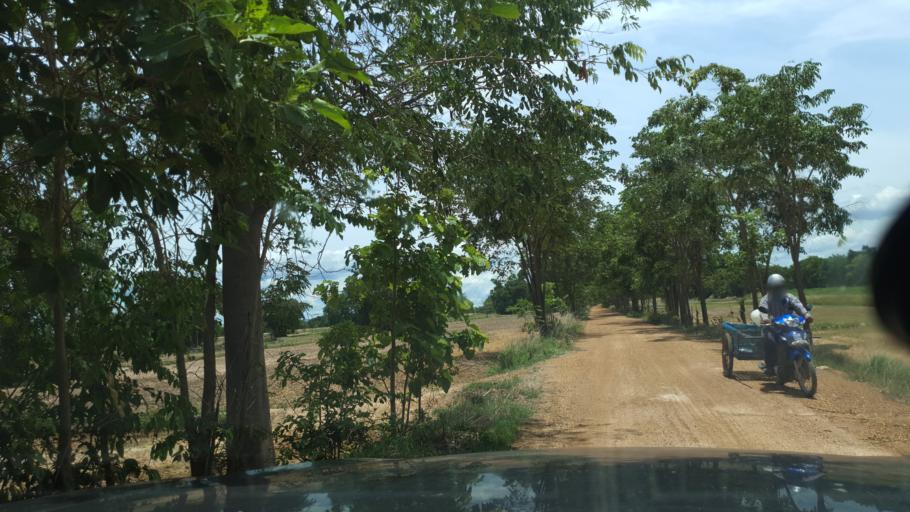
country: TH
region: Sukhothai
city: Ban Na
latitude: 17.1406
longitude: 99.6693
